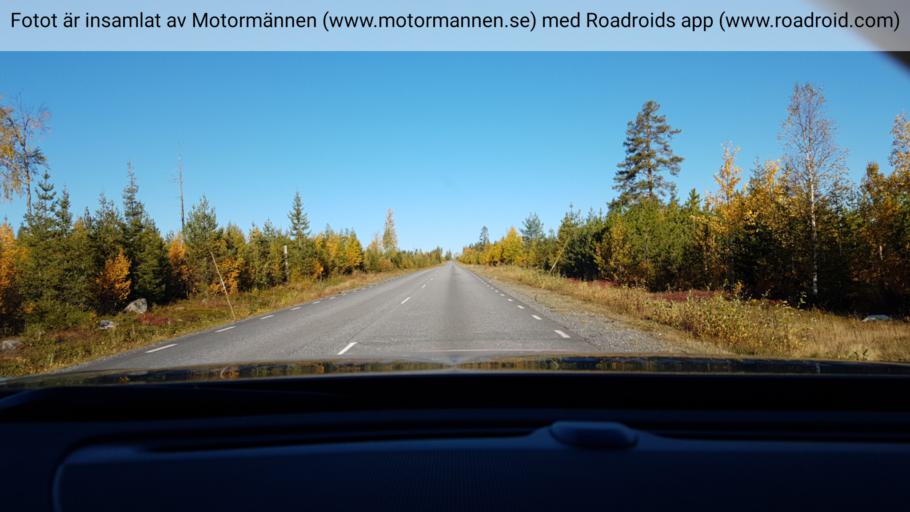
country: SE
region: Vaesterbotten
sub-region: Skelleftea Kommun
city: Storvik
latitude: 65.3443
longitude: 20.5122
